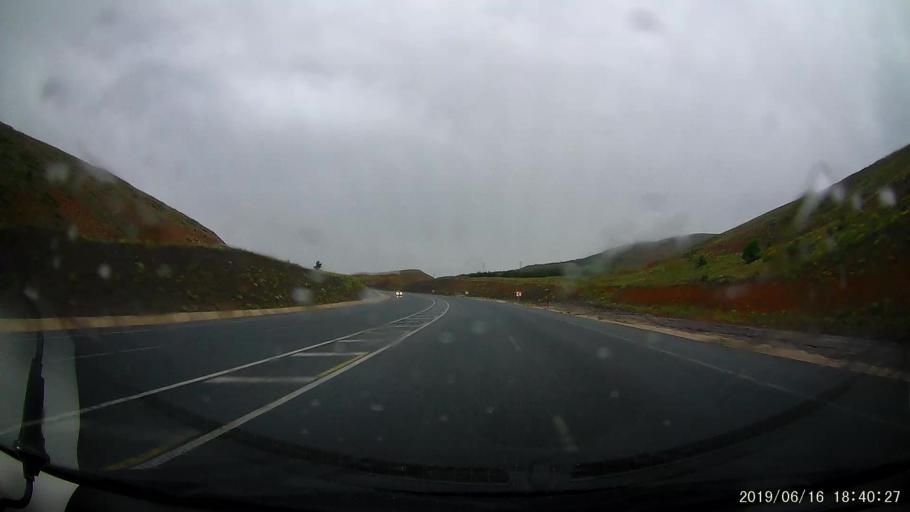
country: TR
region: Erzincan
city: Catalarmut
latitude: 39.8812
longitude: 39.1458
